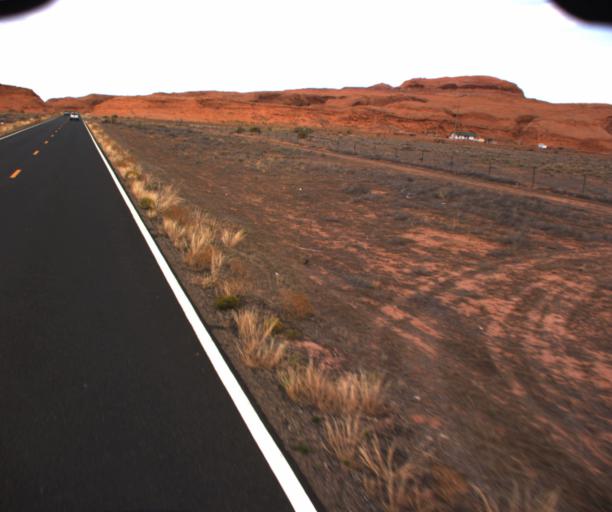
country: US
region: Arizona
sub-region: Apache County
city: Many Farms
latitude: 36.7597
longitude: -109.6493
